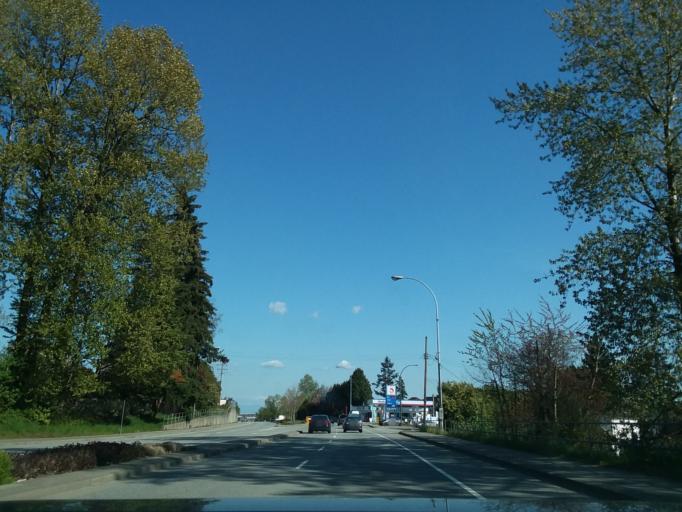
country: CA
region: British Columbia
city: New Westminster
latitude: 49.2382
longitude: -122.8785
